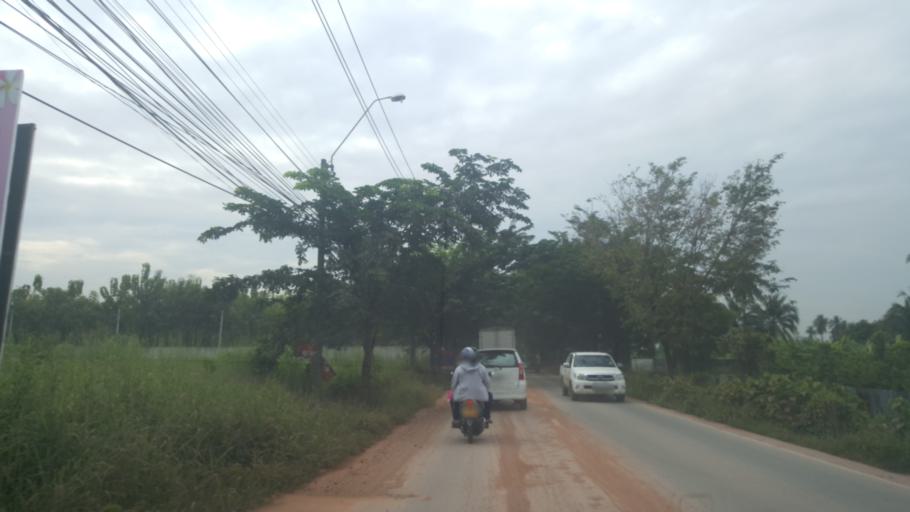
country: TH
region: Bangkok
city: Bang Khae
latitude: 13.6859
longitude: 100.3921
